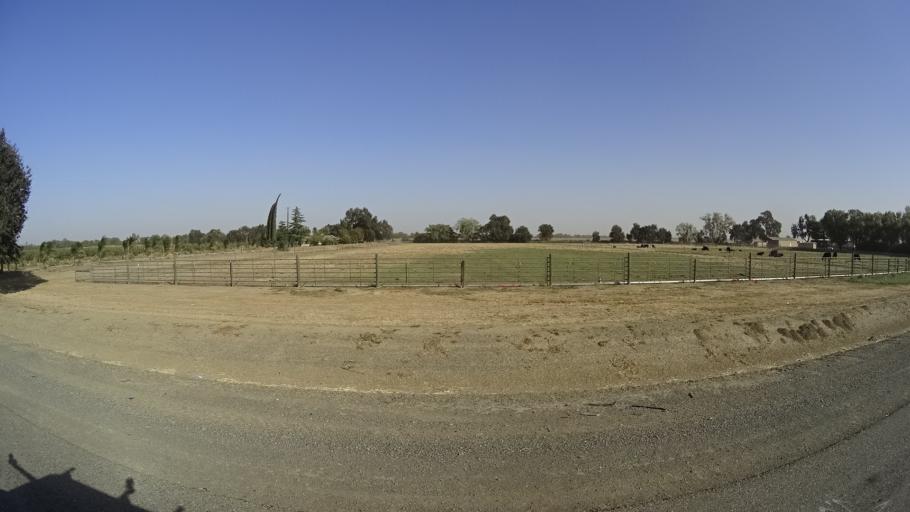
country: US
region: California
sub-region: Yolo County
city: Woodland
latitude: 38.7847
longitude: -121.7284
